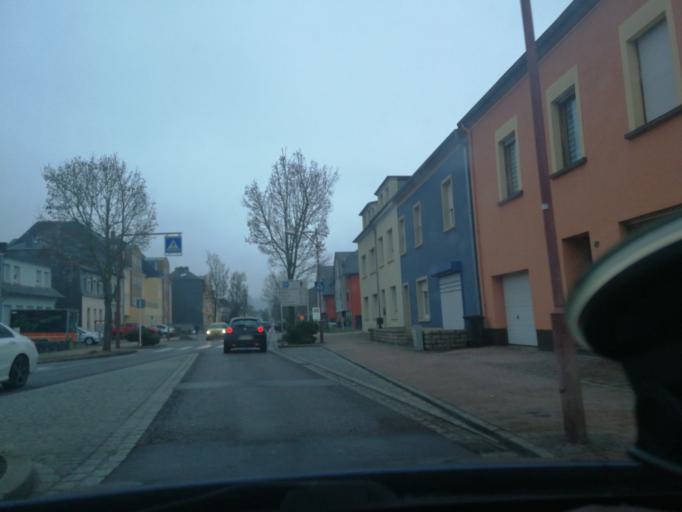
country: LU
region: Grevenmacher
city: Wasserbillig
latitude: 49.7100
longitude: 6.4919
